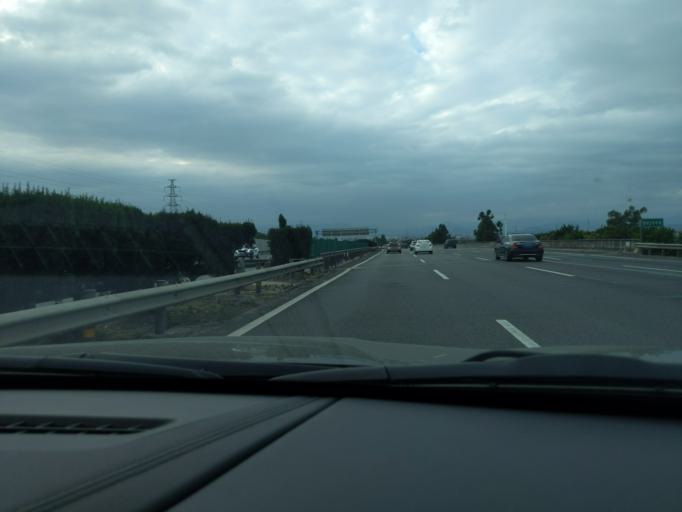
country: CN
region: Fujian
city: Maxiang
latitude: 24.6890
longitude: 118.2476
